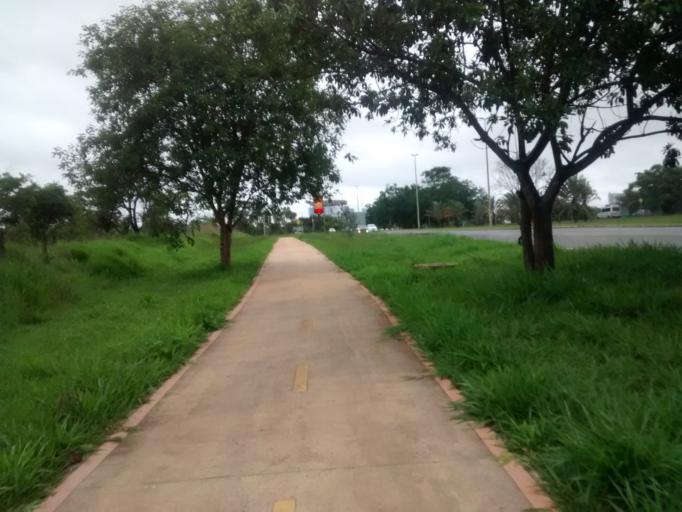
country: BR
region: Federal District
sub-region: Brasilia
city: Brasilia
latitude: -15.8037
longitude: -47.8513
